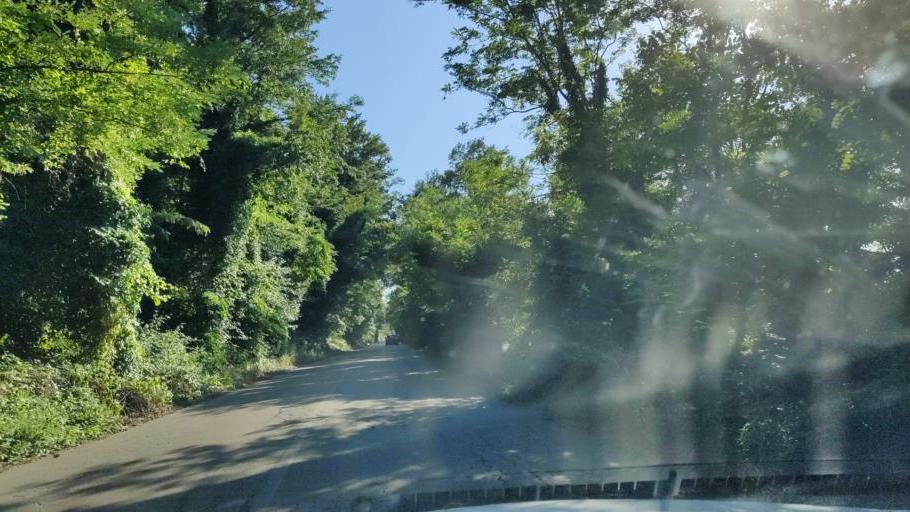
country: IT
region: Umbria
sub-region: Provincia di Terni
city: Penna in Teverina
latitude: 42.4779
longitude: 12.3715
